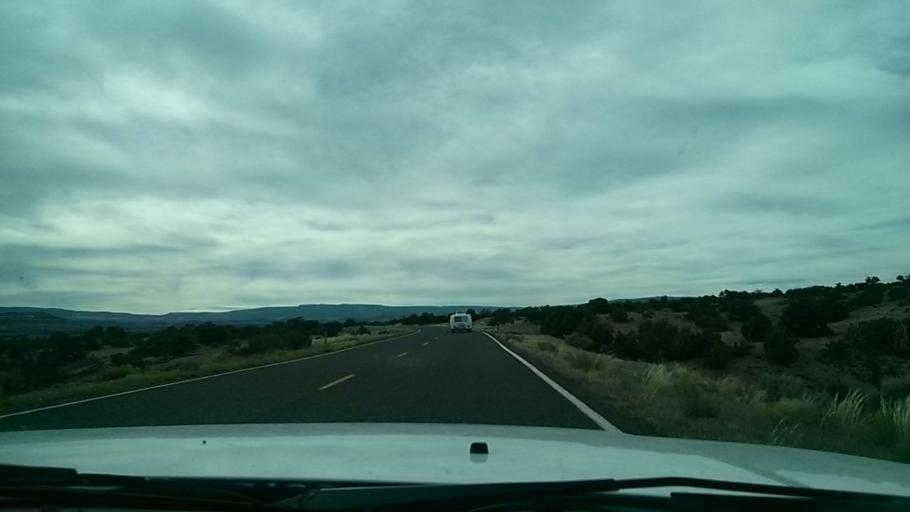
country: US
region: Utah
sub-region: Wayne County
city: Loa
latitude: 37.7355
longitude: -111.5435
